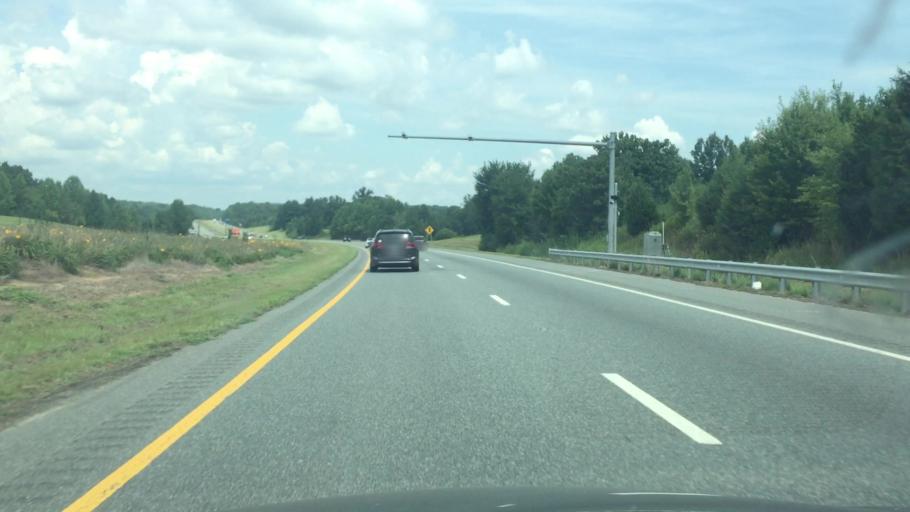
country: US
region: North Carolina
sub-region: Montgomery County
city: Biscoe
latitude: 35.4896
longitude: -79.7801
